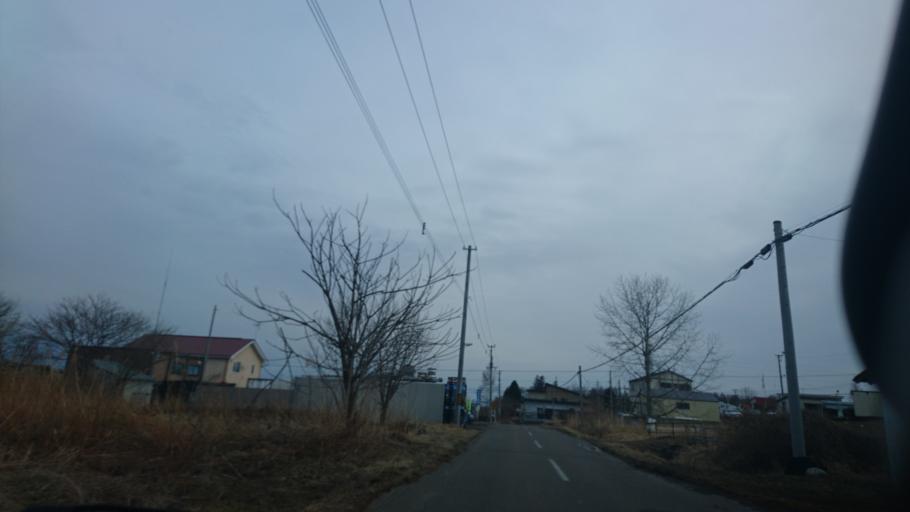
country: JP
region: Hokkaido
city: Otofuke
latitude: 42.9784
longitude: 143.2048
